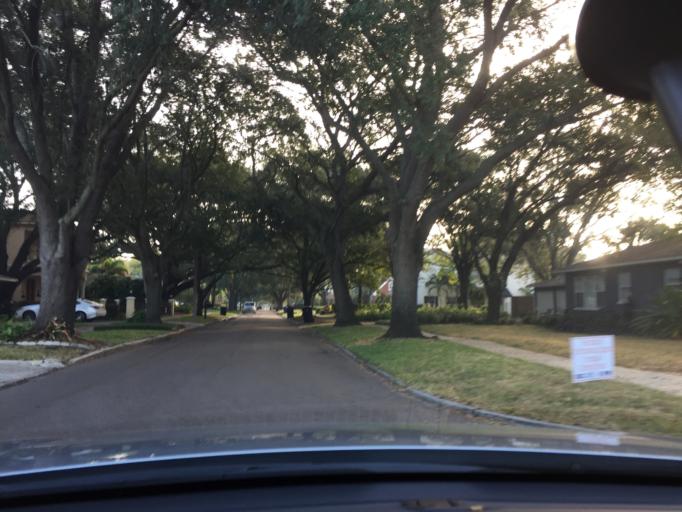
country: US
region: Florida
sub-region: Hillsborough County
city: Tampa
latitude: 27.9369
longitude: -82.4924
